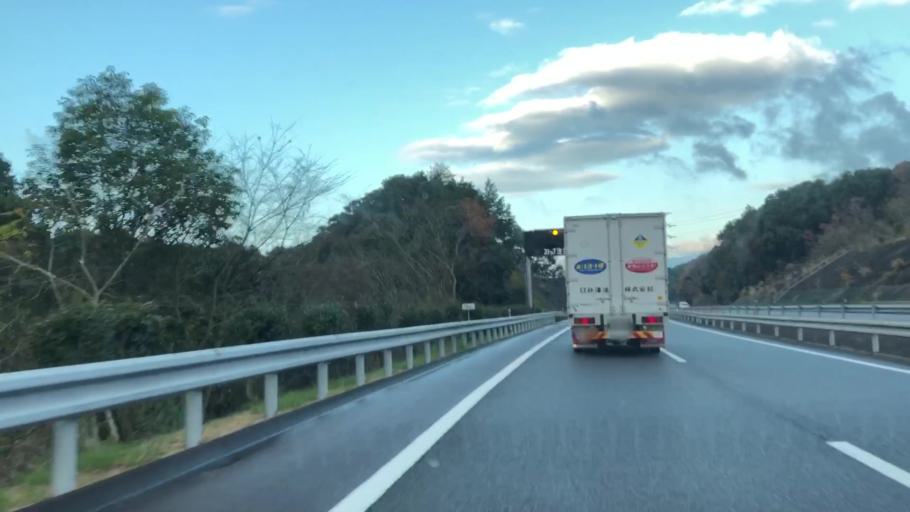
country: JP
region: Saga Prefecture
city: Ureshinomachi-shimojuku
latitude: 33.1561
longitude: 129.9008
